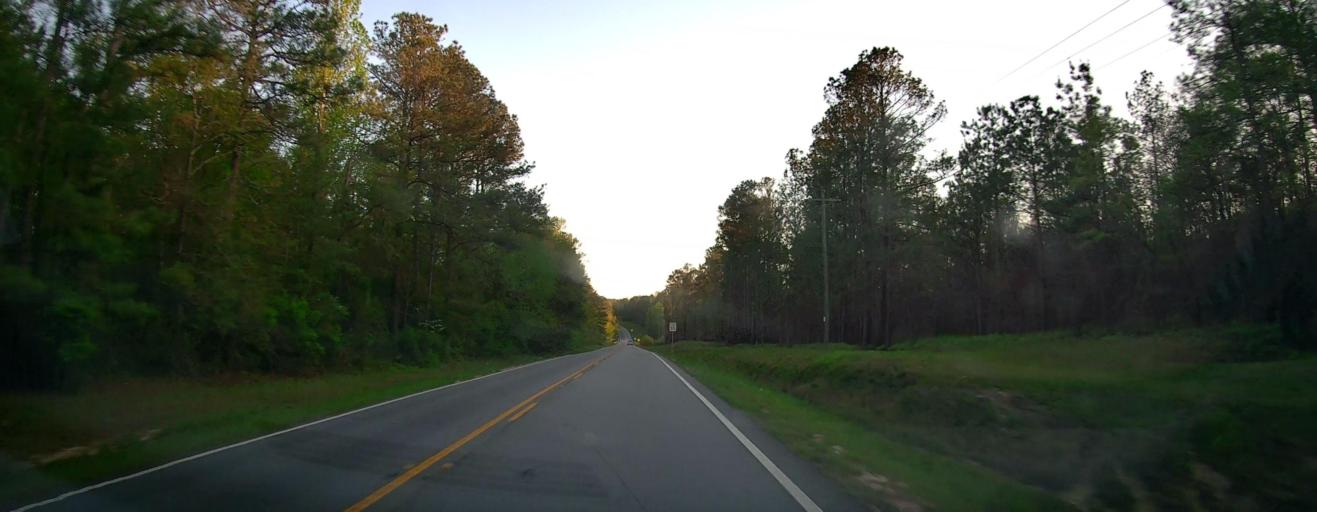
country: US
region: Georgia
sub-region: Talbot County
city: Talbotton
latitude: 32.5180
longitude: -84.6049
